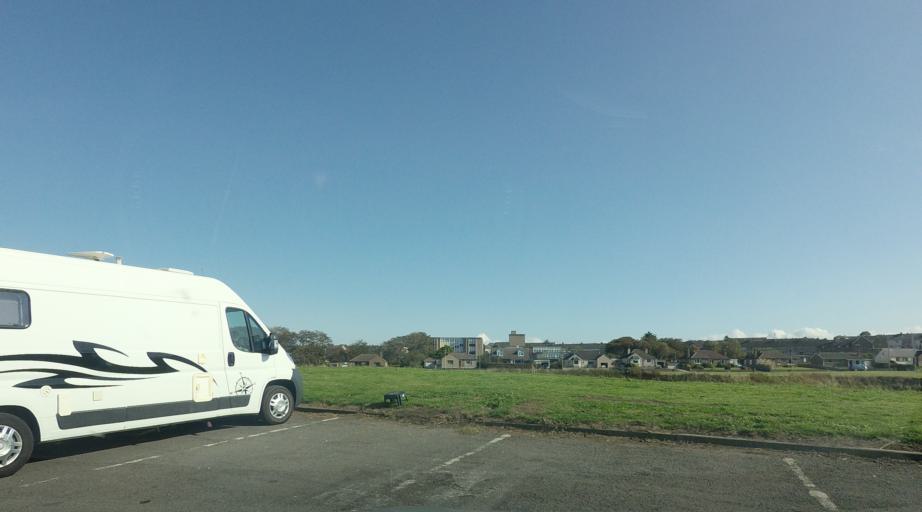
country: GB
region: Scotland
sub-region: Highland
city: Thurso
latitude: 58.5948
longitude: -3.5155
